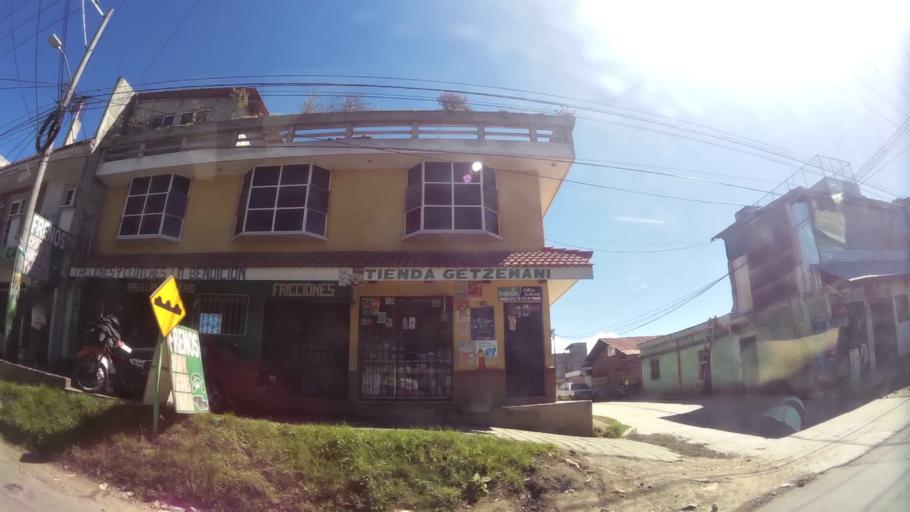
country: GT
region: Guatemala
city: San Jose Pinula
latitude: 14.5474
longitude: -90.4088
